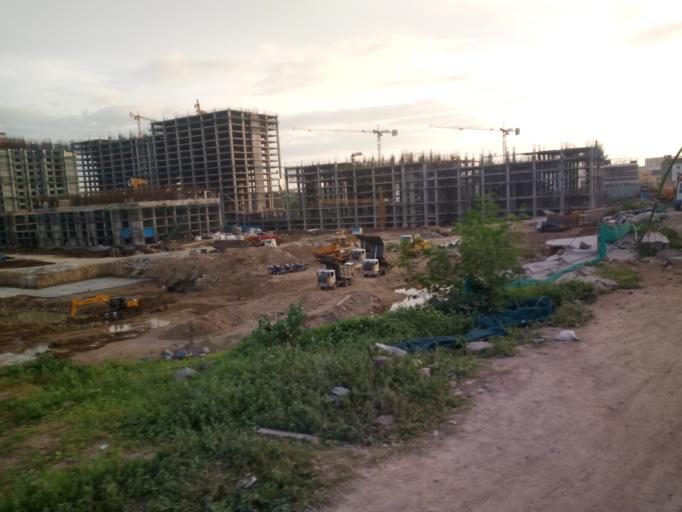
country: IN
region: Telangana
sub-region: Rangareddi
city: Kukatpalli
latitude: 17.4338
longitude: 78.3778
